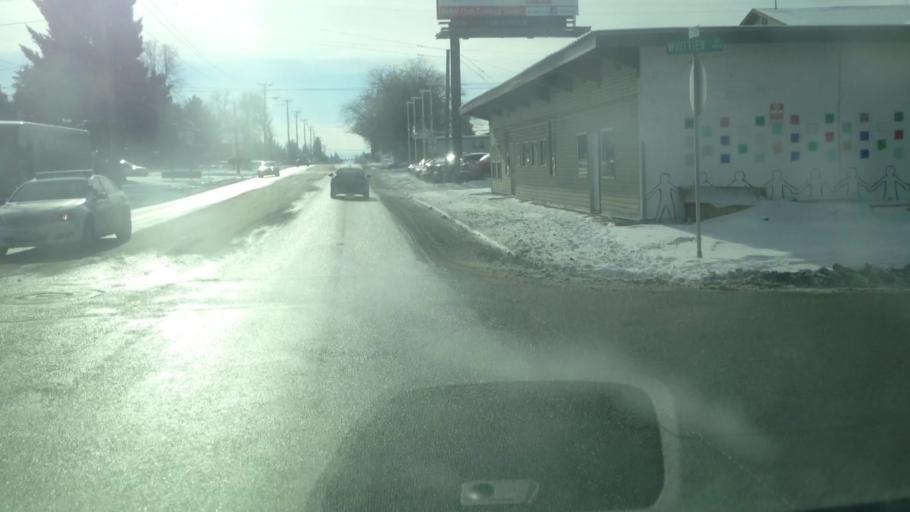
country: US
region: Idaho
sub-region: Bonneville County
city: Idaho Falls
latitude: 43.5032
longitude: -112.0239
